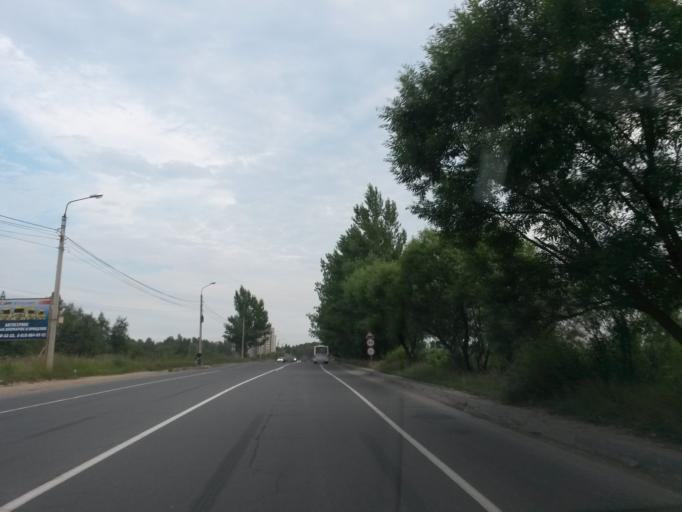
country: RU
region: Jaroslavl
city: Yaroslavl
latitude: 57.5903
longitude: 39.8173
